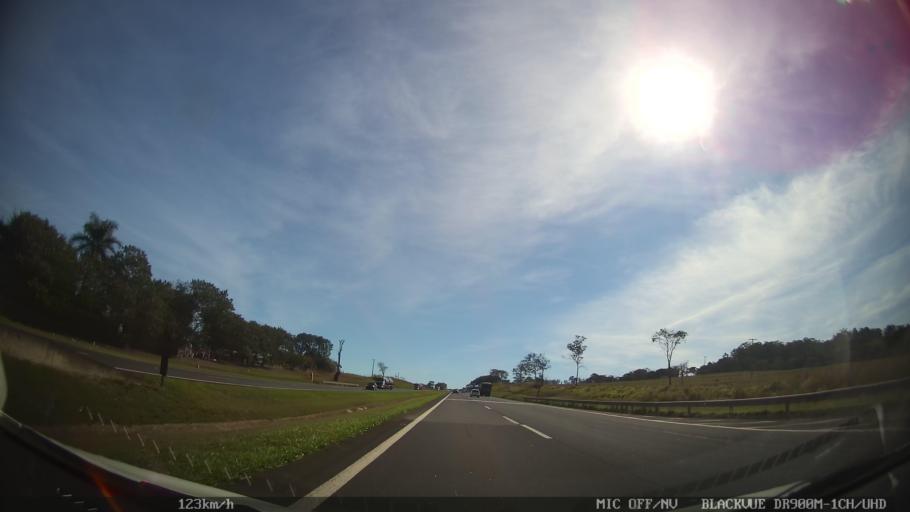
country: BR
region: Sao Paulo
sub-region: Pirassununga
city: Pirassununga
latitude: -22.0474
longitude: -47.4299
